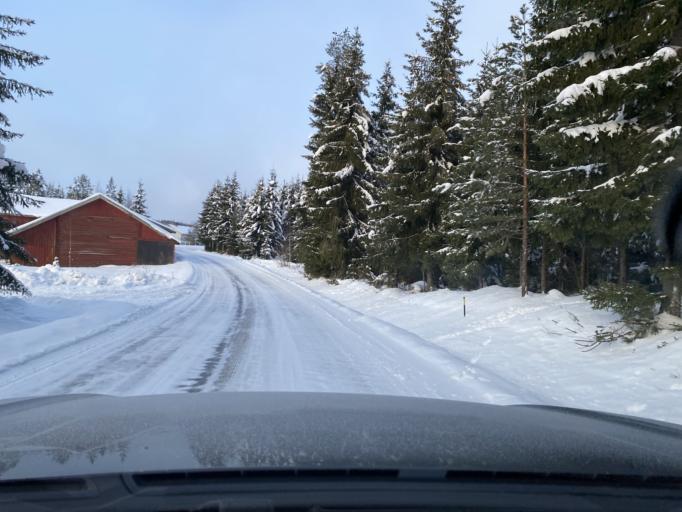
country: FI
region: Haeme
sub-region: Forssa
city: Tammela
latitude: 60.8633
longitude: 23.8857
